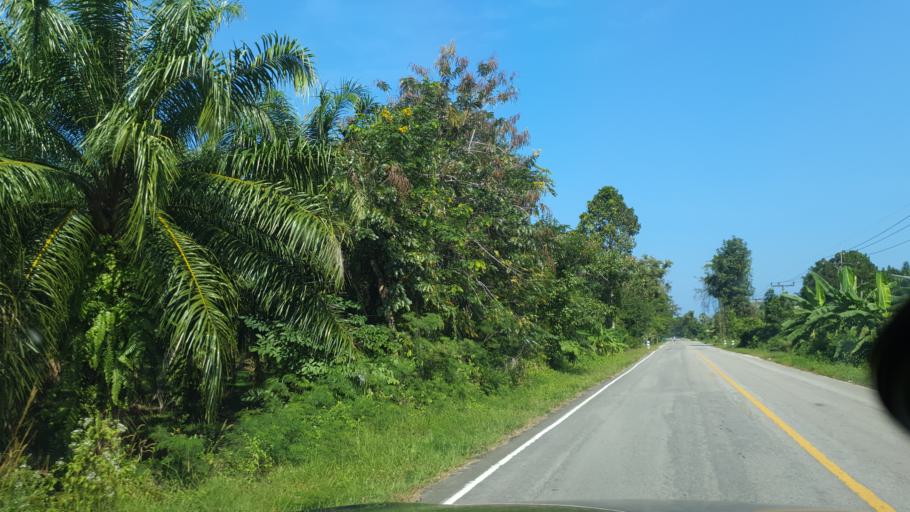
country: TH
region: Surat Thani
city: Tha Chana
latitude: 9.5790
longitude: 99.1892
